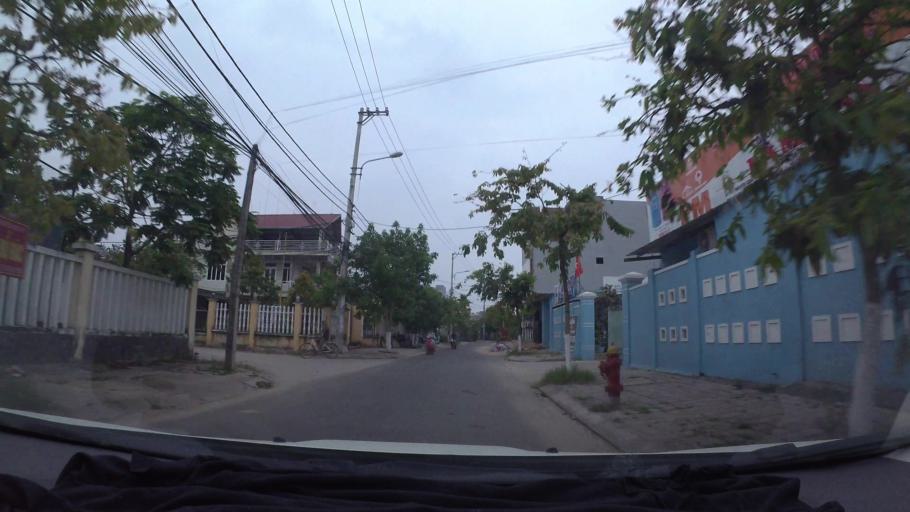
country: VN
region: Da Nang
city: Thanh Khe
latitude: 16.0480
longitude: 108.1763
